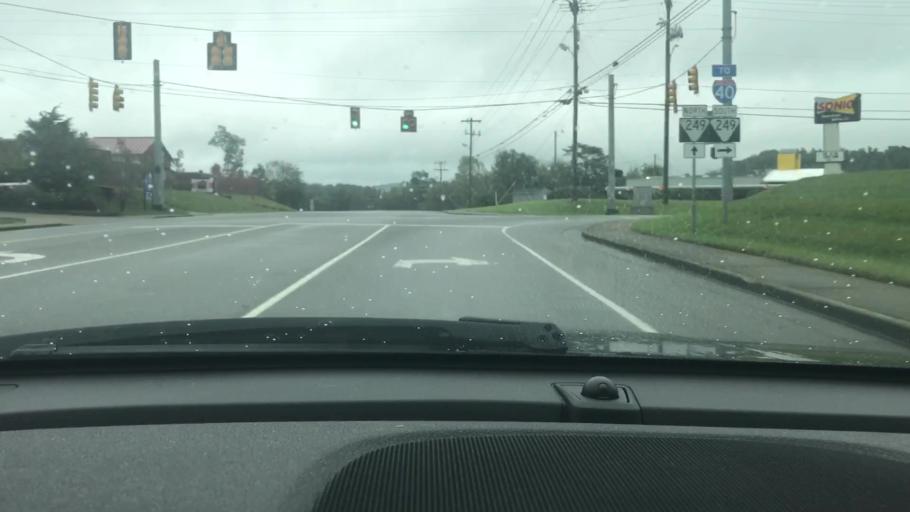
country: US
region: Tennessee
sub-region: Cheatham County
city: Kingston Springs
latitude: 36.0873
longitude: -87.1013
